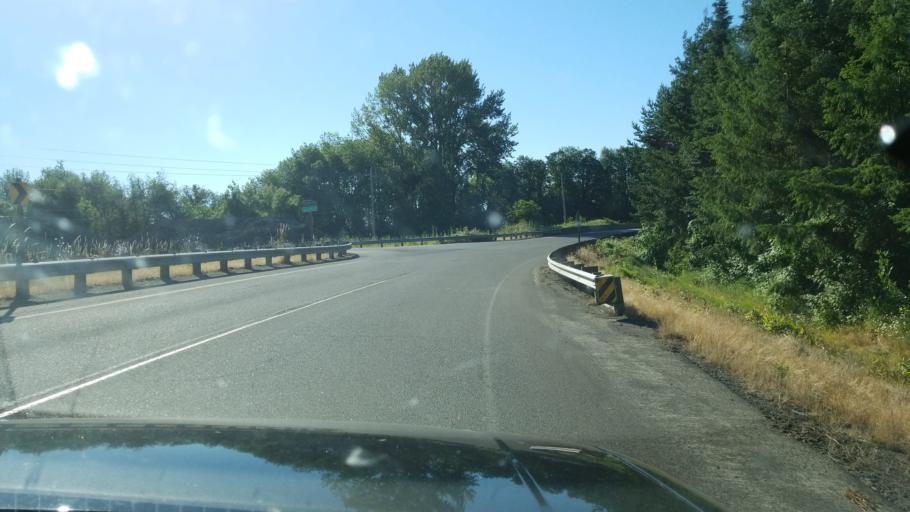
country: US
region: Oregon
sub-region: Yamhill County
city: McMinnville
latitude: 45.2304
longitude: -123.2327
